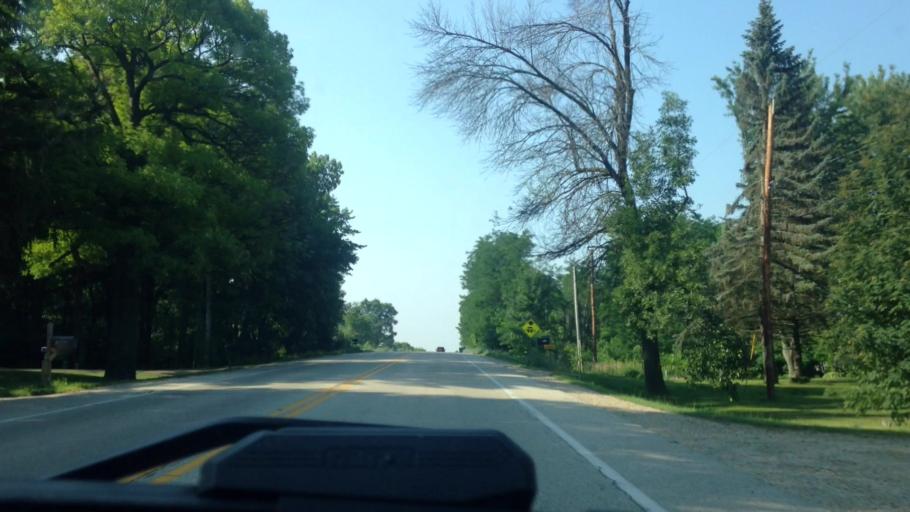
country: US
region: Wisconsin
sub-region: Washington County
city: Slinger
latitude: 43.3045
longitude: -88.2608
